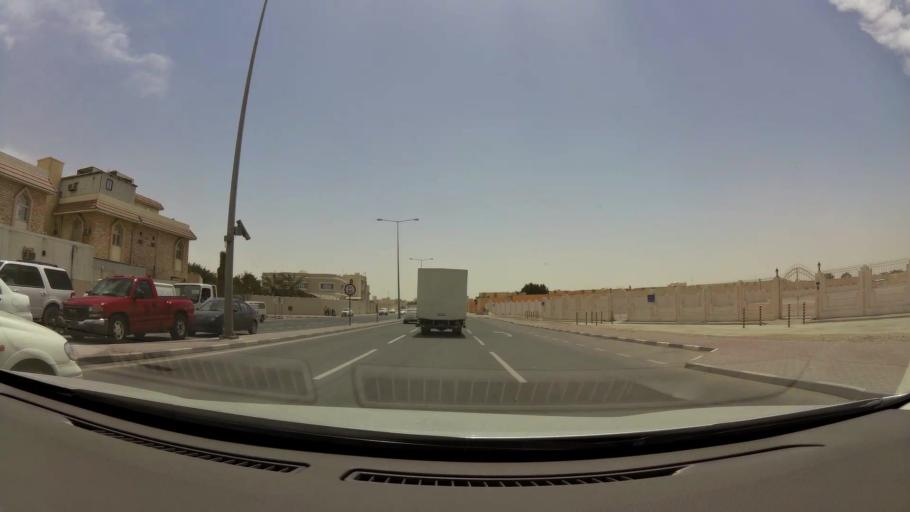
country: QA
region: Baladiyat ar Rayyan
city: Ar Rayyan
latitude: 25.2661
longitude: 51.4202
